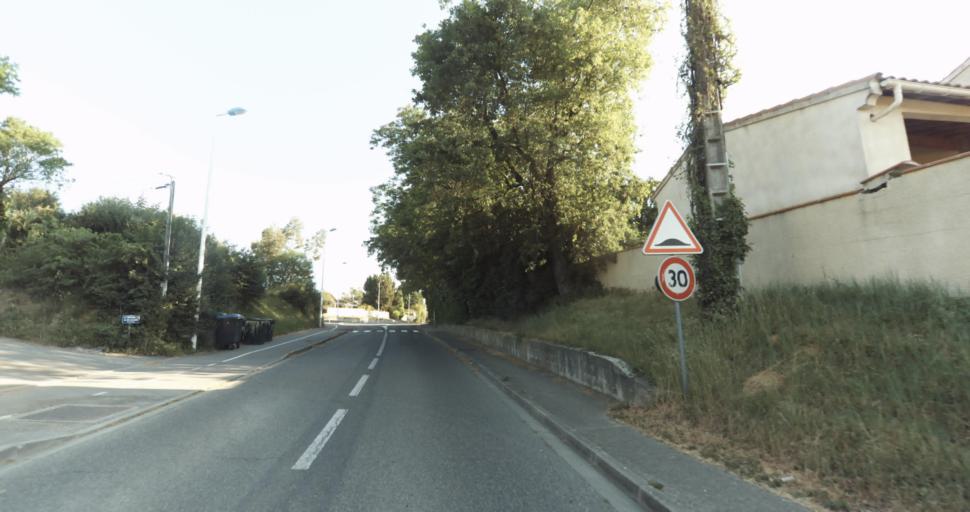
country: FR
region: Midi-Pyrenees
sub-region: Departement de la Haute-Garonne
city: Leguevin
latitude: 43.6023
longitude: 1.2332
